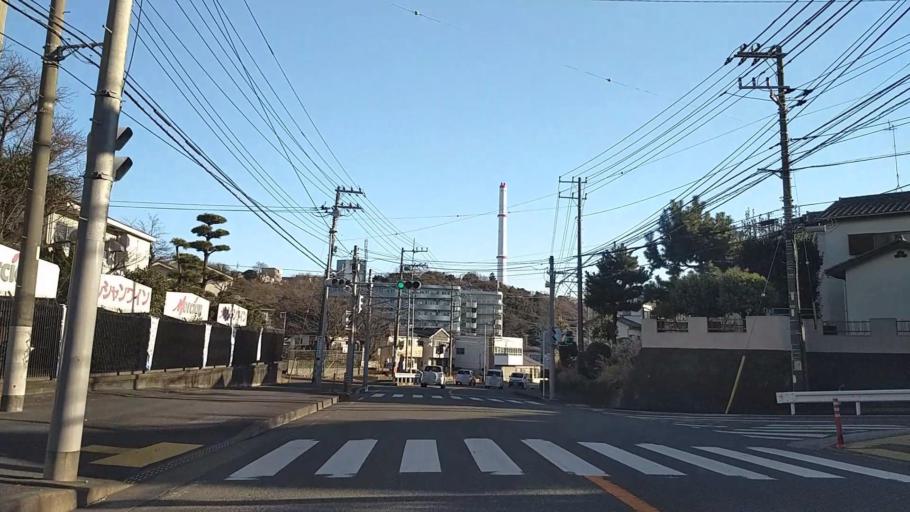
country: JP
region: Kanagawa
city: Fujisawa
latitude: 35.3468
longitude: 139.4643
